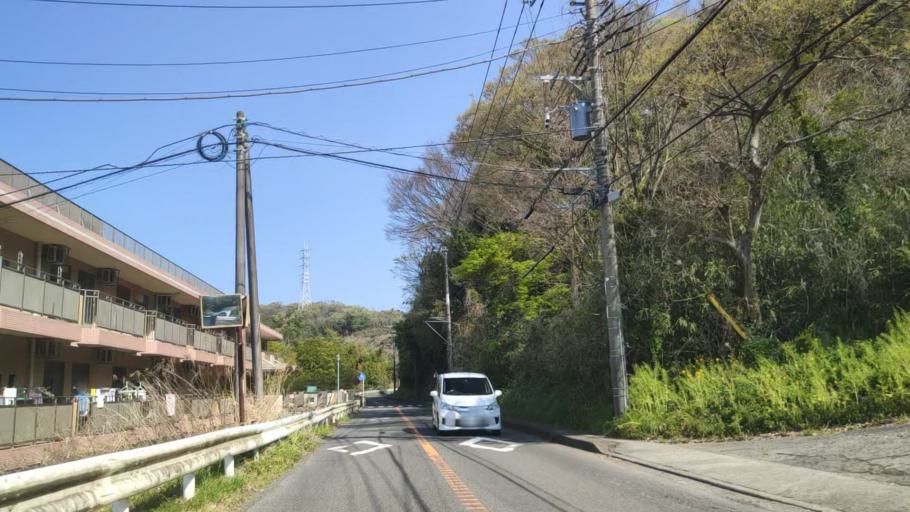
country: JP
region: Kanagawa
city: Ninomiya
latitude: 35.3159
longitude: 139.2730
